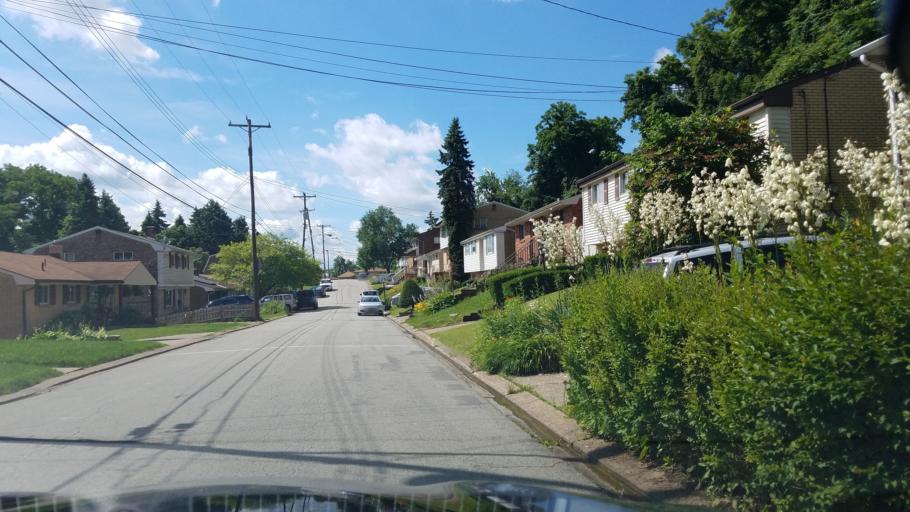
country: US
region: Pennsylvania
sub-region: Allegheny County
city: Rankin
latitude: 40.4175
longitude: -79.8733
